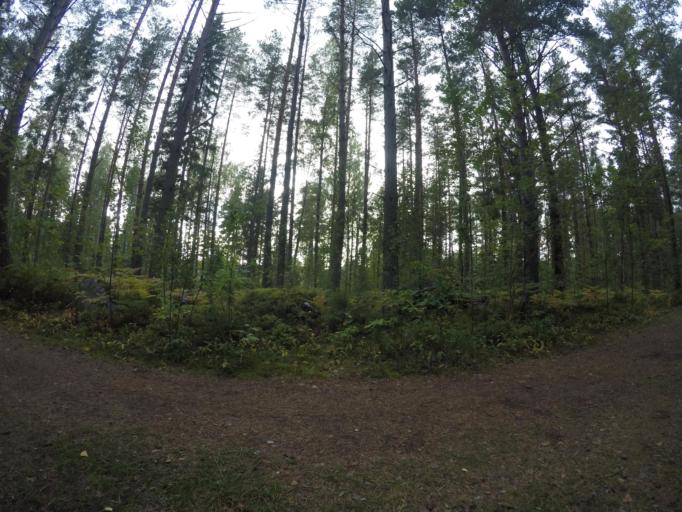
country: SE
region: Vaestmanland
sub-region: Vasteras
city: Vasteras
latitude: 59.6404
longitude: 16.5207
